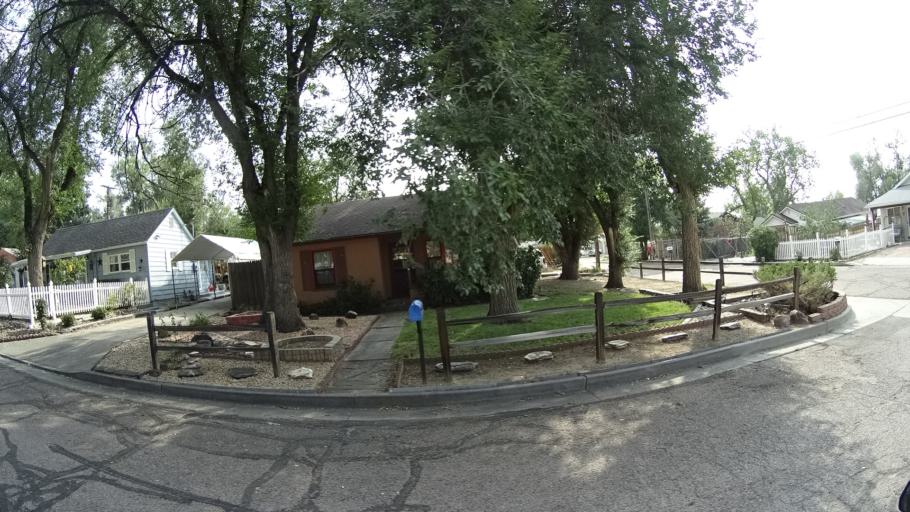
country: US
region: Colorado
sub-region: El Paso County
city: Colorado Springs
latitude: 38.8482
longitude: -104.7820
